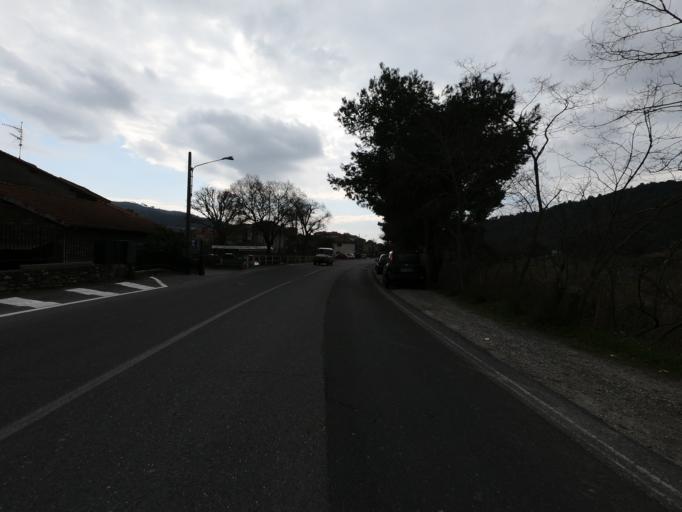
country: IT
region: Liguria
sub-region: Provincia di Imperia
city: Villa Faraldi
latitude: 43.9919
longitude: 8.1213
